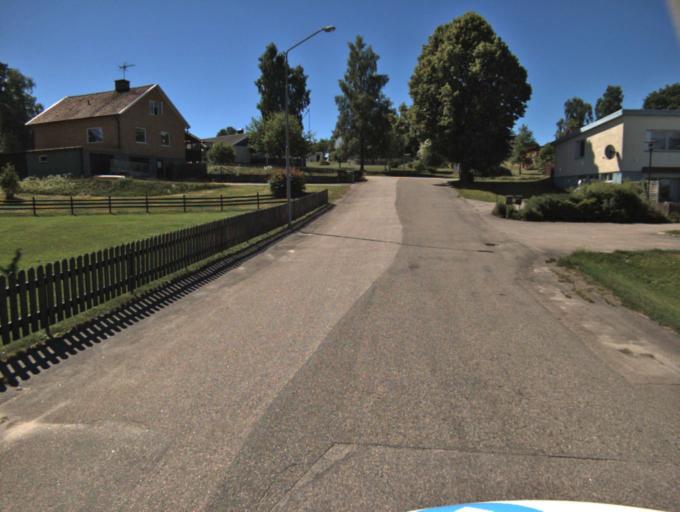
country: SE
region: Vaestra Goetaland
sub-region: Ulricehamns Kommun
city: Ulricehamn
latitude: 57.6676
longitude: 13.4349
